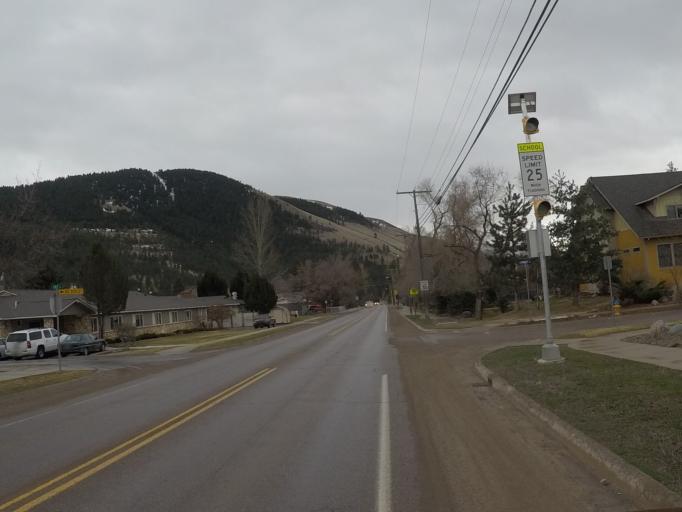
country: US
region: Montana
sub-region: Missoula County
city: East Missoula
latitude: 46.8940
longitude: -113.9657
